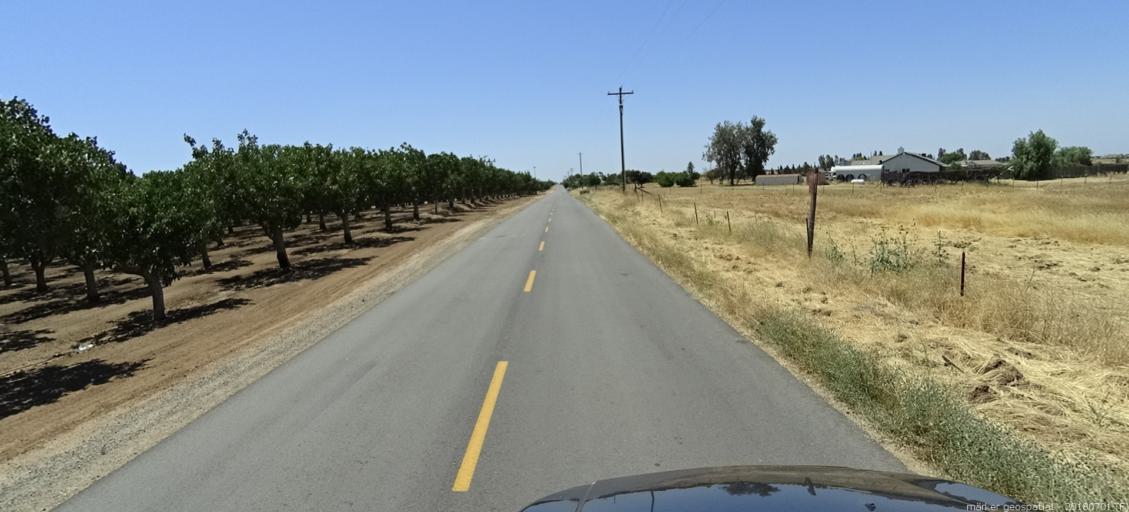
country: US
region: California
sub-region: Madera County
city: Madera Acres
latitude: 37.0637
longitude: -120.0020
